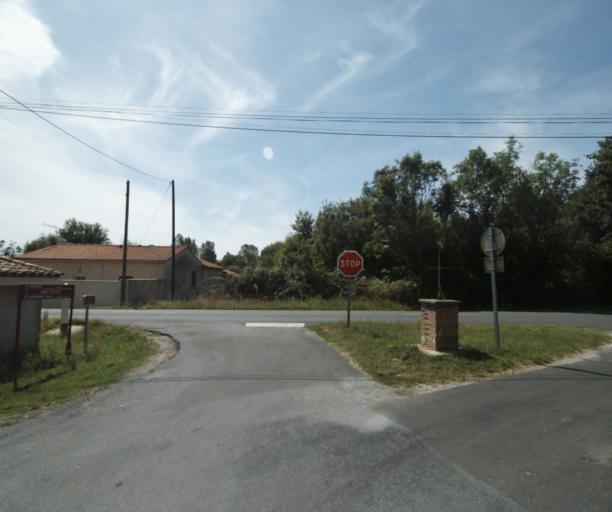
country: FR
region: Midi-Pyrenees
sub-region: Departement du Tarn
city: Puylaurens
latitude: 43.5398
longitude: 2.0108
